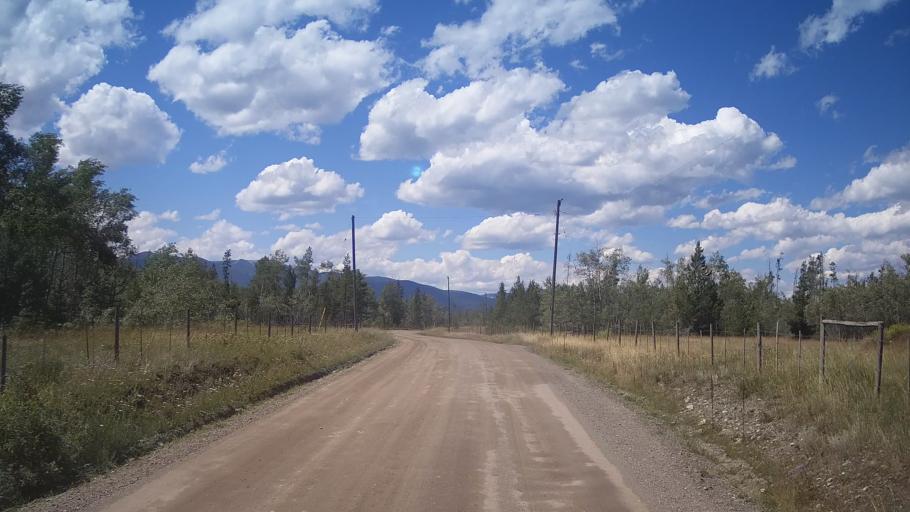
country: CA
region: British Columbia
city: Cache Creek
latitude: 51.2581
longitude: -121.6839
